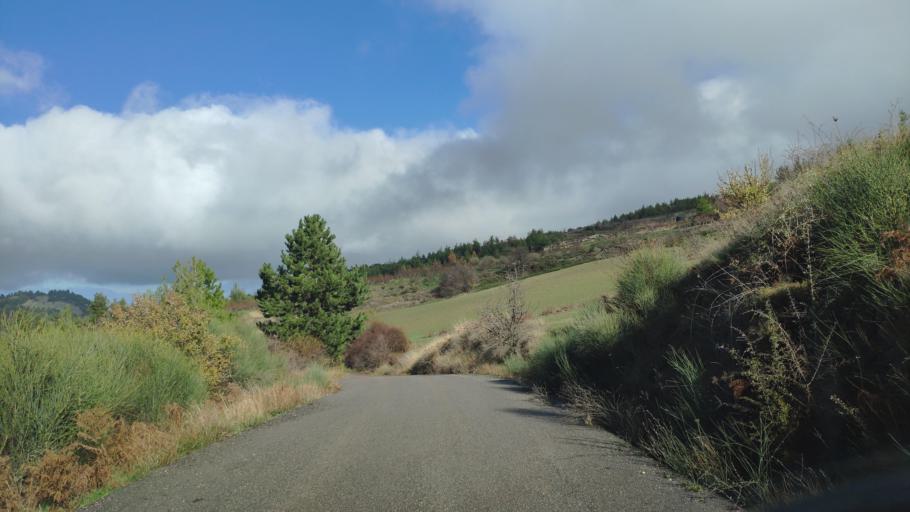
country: GR
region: West Greece
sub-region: Nomos Achaias
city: Aiyira
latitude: 38.0713
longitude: 22.4680
